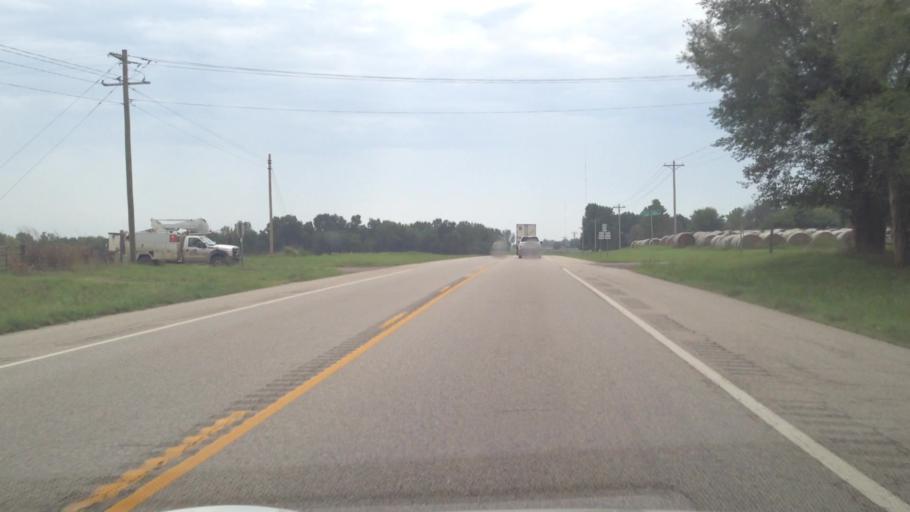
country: US
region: Missouri
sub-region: Jasper County
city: Carl Junction
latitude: 37.2518
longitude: -94.7052
